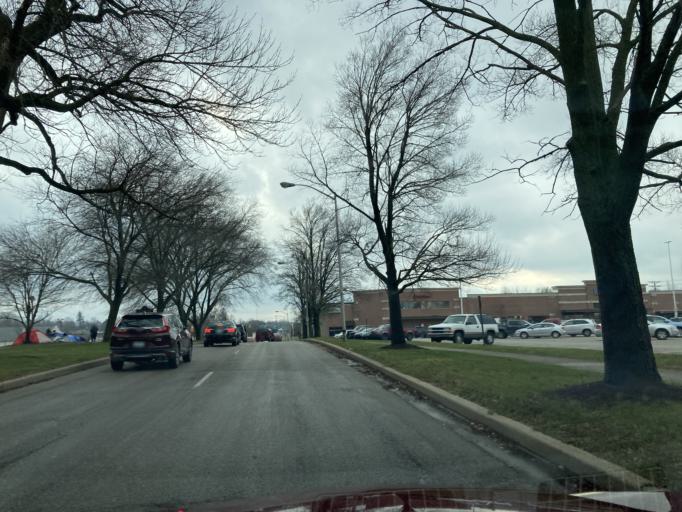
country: US
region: Indiana
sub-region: Monroe County
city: Bloomington
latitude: 39.1612
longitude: -86.5350
